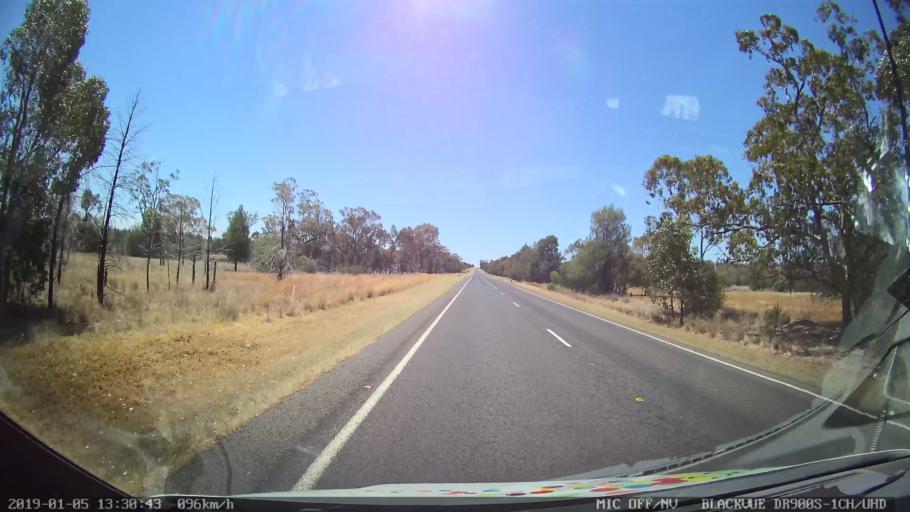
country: AU
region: New South Wales
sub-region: Gunnedah
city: Gunnedah
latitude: -31.0165
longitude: 150.0745
